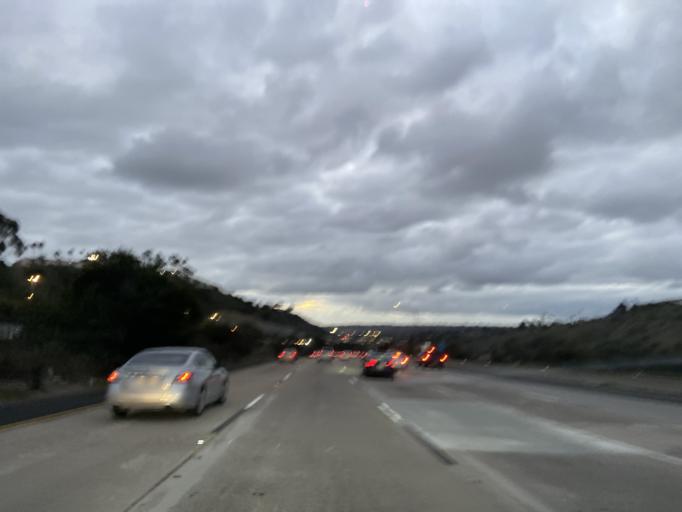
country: US
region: California
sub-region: San Diego County
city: La Mesa
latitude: 32.7802
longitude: -117.0728
